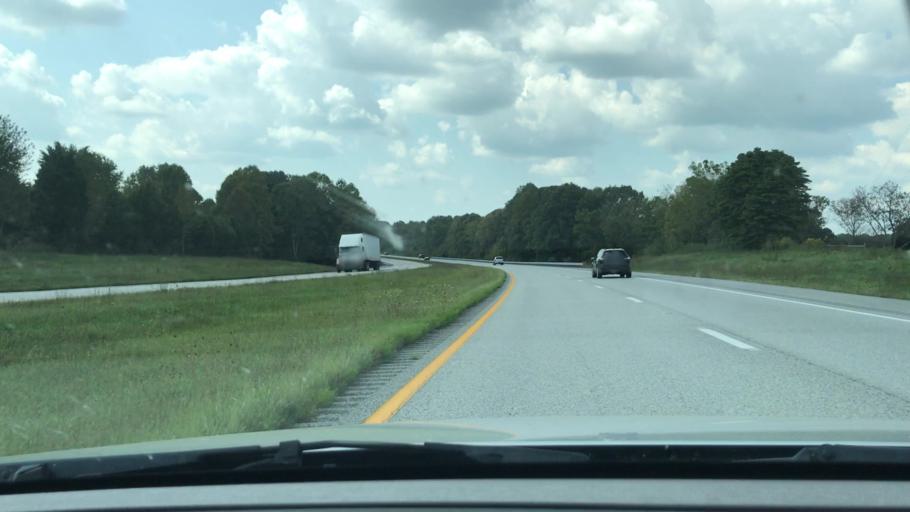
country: US
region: Kentucky
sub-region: Russell County
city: Russell Springs
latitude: 37.0881
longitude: -84.9125
